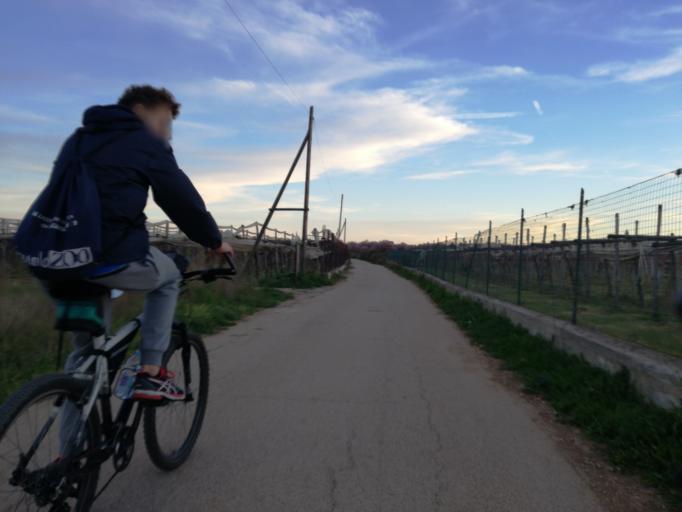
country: IT
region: Apulia
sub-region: Provincia di Bari
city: Adelfia
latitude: 41.0120
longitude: 16.8716
